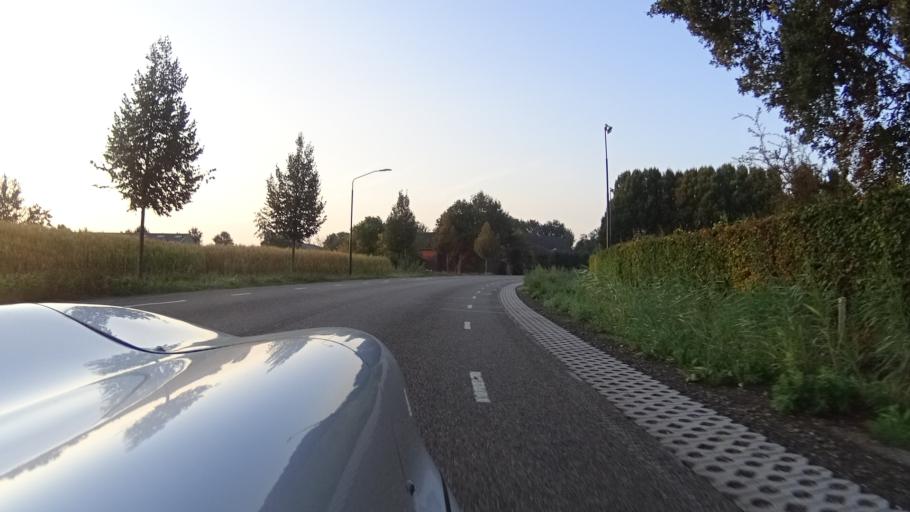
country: NL
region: North Brabant
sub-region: Gemeente Sint Anthonis
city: Sint Anthonis
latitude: 51.6231
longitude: 5.8961
